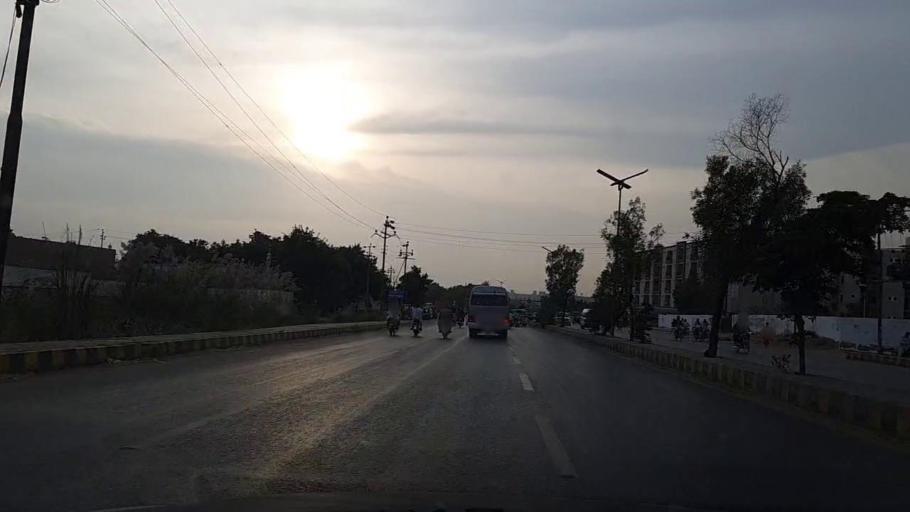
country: PK
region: Sindh
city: Malir Cantonment
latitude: 24.8552
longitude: 67.2550
